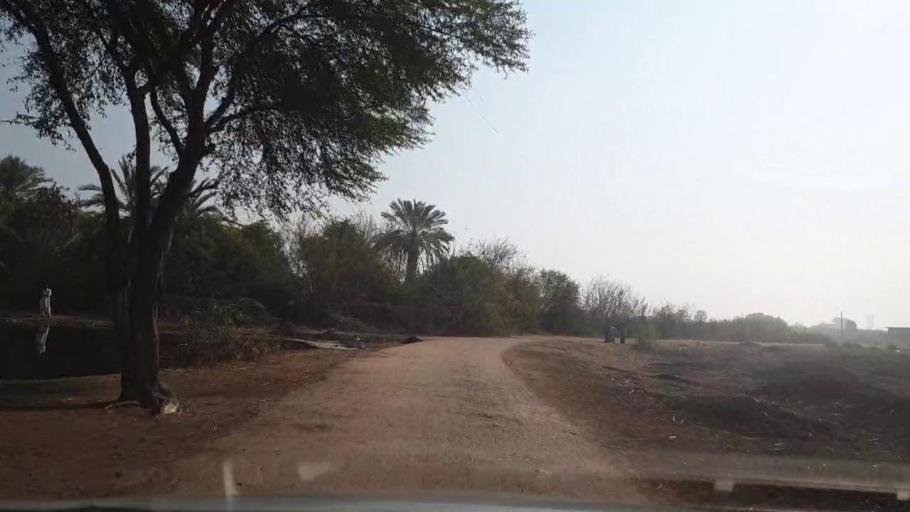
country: PK
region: Sindh
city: Matiari
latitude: 25.5698
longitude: 68.4945
